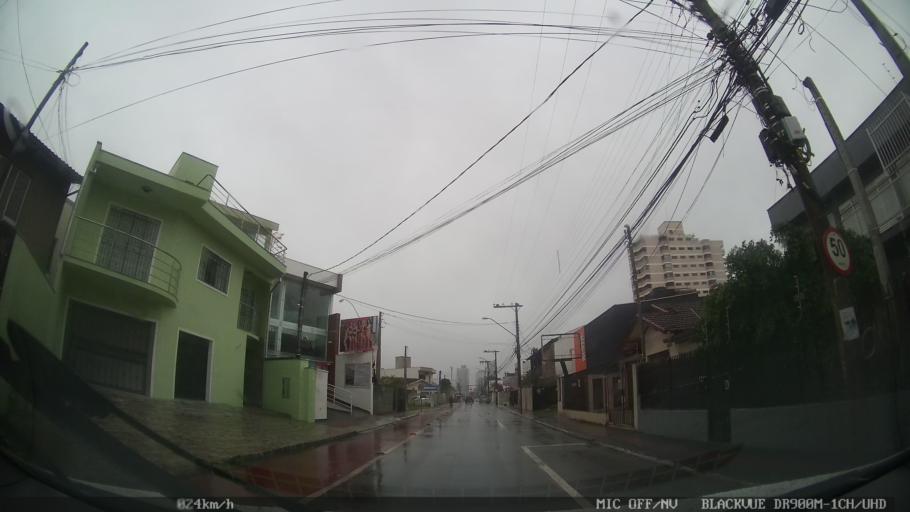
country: BR
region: Santa Catarina
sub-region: Itajai
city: Itajai
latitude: -26.9089
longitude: -48.6675
